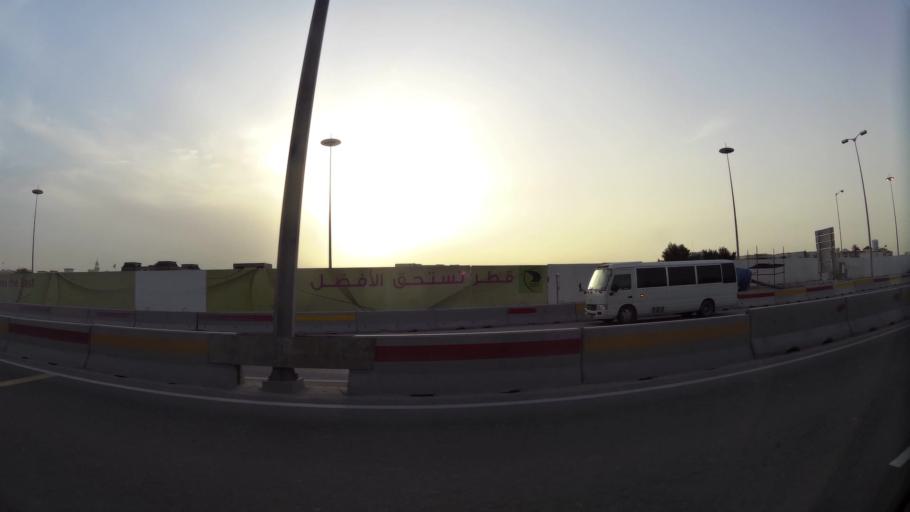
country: QA
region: Baladiyat ad Dawhah
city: Doha
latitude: 25.3573
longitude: 51.5210
